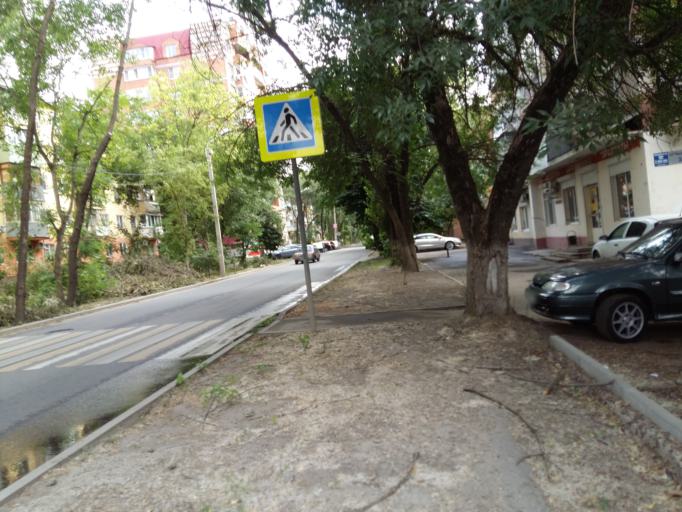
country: RU
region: Rostov
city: Imeni Chkalova
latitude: 47.2779
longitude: 39.7360
